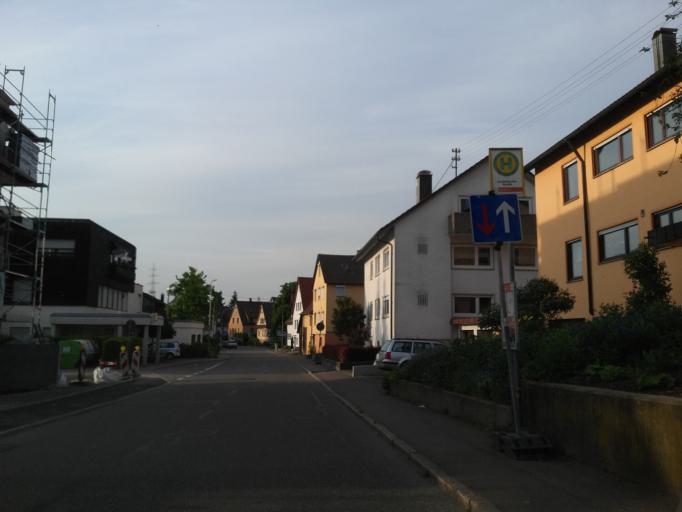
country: DE
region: Baden-Wuerttemberg
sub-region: Regierungsbezirk Stuttgart
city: Leutenbach
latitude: 48.9009
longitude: 9.4050
